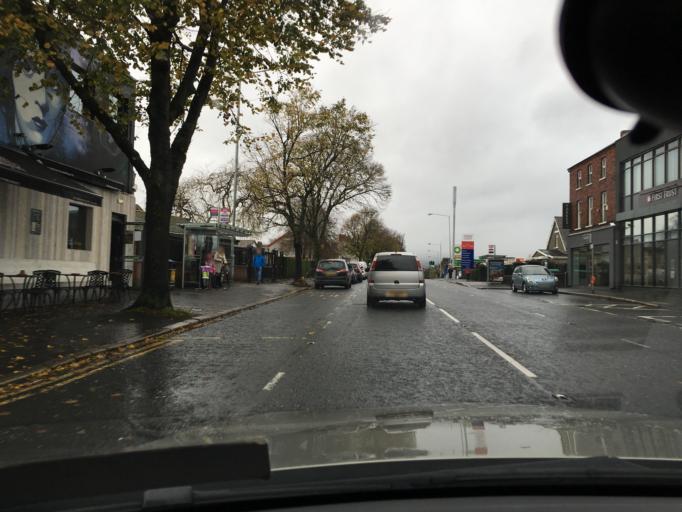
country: GB
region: Northern Ireland
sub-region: Castlereagh District
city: Castlereagh
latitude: 54.5953
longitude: -5.8702
